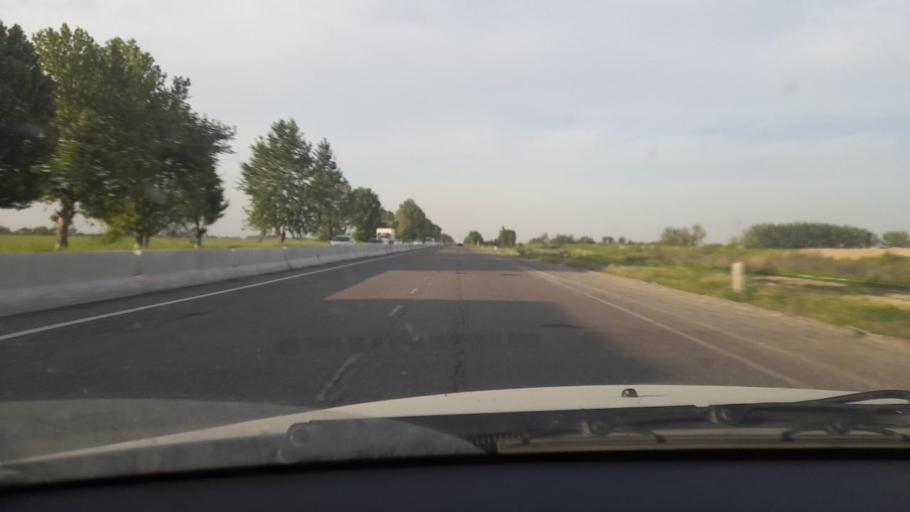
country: UZ
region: Jizzax
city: Gagarin
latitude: 40.5402
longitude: 68.3508
